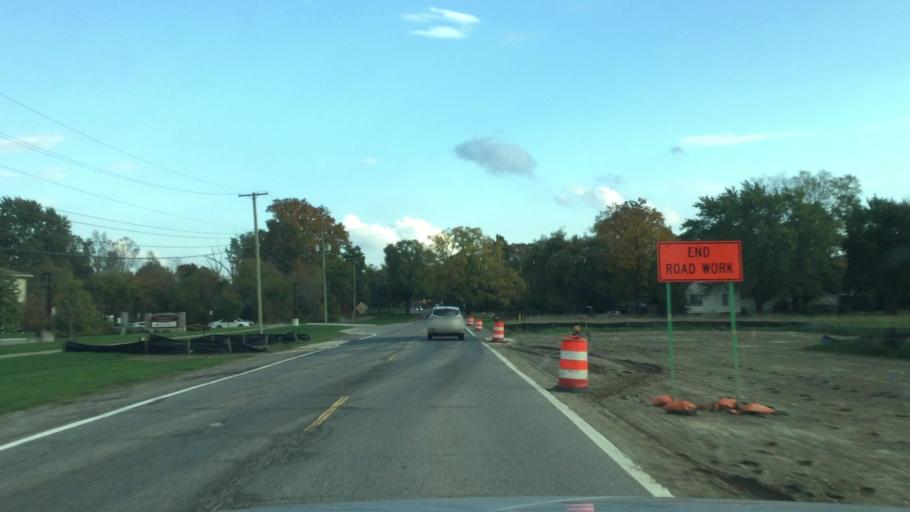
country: US
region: Michigan
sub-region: Oakland County
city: Wolverine Lake
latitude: 42.6448
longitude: -83.5001
